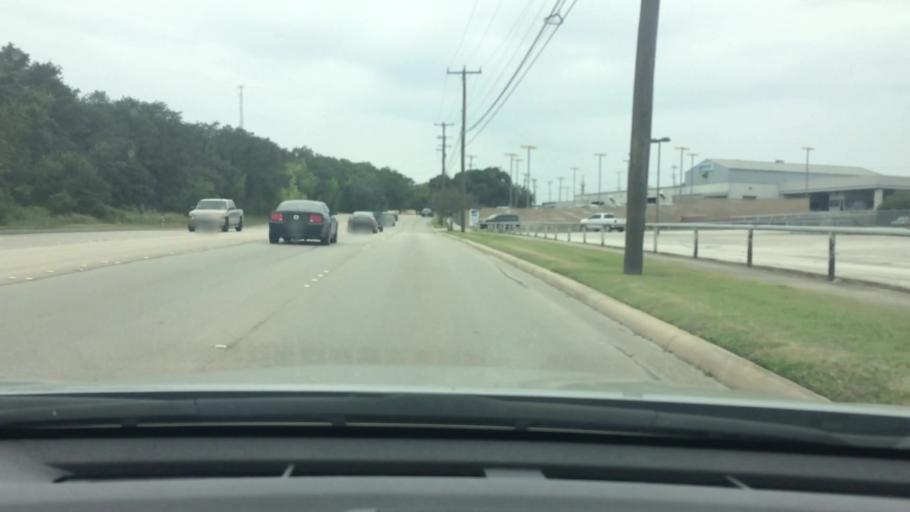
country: US
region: Texas
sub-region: Bexar County
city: Live Oak
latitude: 29.5509
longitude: -98.3518
